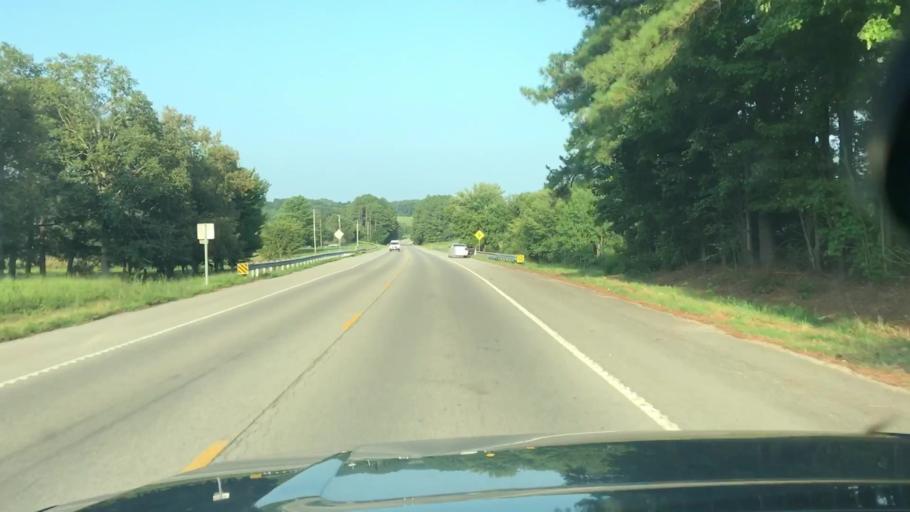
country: US
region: Tennessee
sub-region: Sumner County
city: Portland
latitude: 36.5788
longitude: -86.4253
